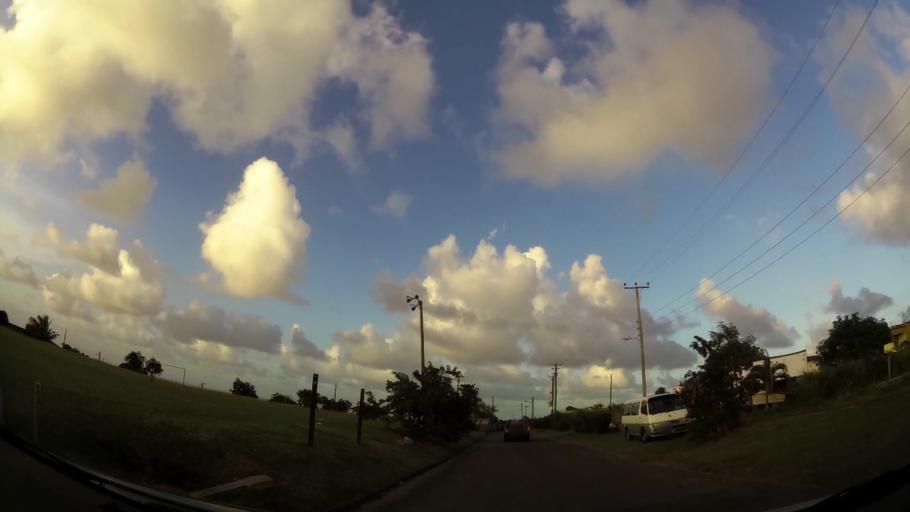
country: KN
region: Saint Paul Capesterre
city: Saint Paul's
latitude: 17.4041
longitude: -62.8365
